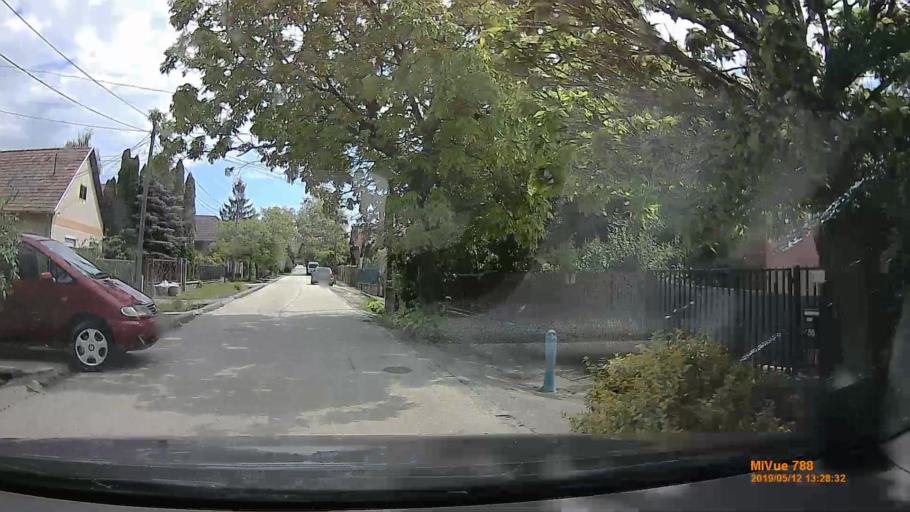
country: HU
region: Budapest
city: Budapest XVII. keruelet
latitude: 47.4810
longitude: 19.2942
